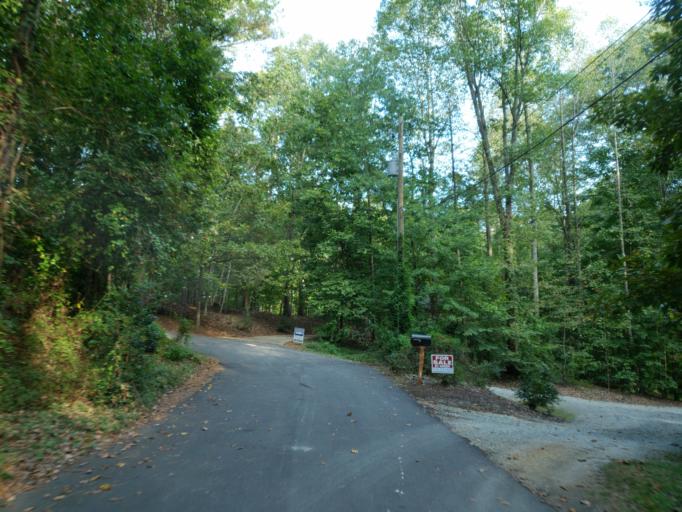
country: US
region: Georgia
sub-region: Fulton County
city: Roswell
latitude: 34.0793
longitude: -84.4074
